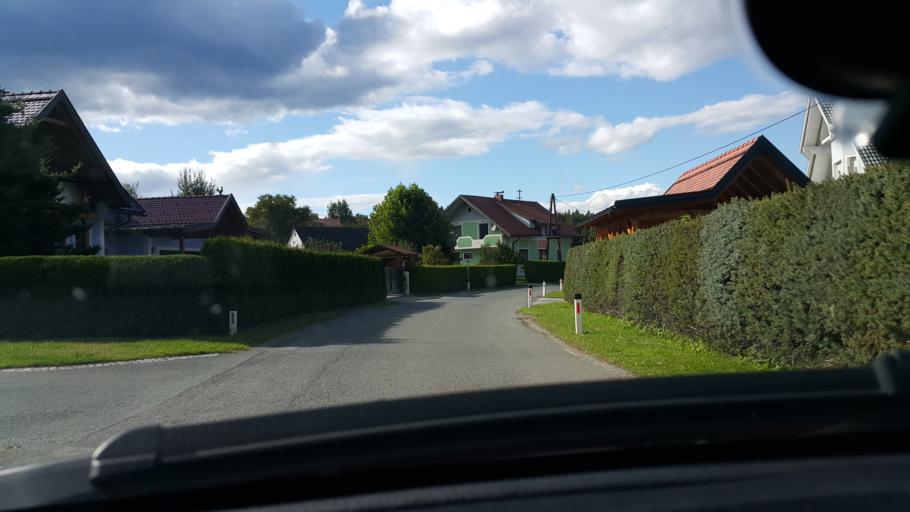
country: AT
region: Styria
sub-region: Politischer Bezirk Deutschlandsberg
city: Wies
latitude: 46.7372
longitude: 15.2856
